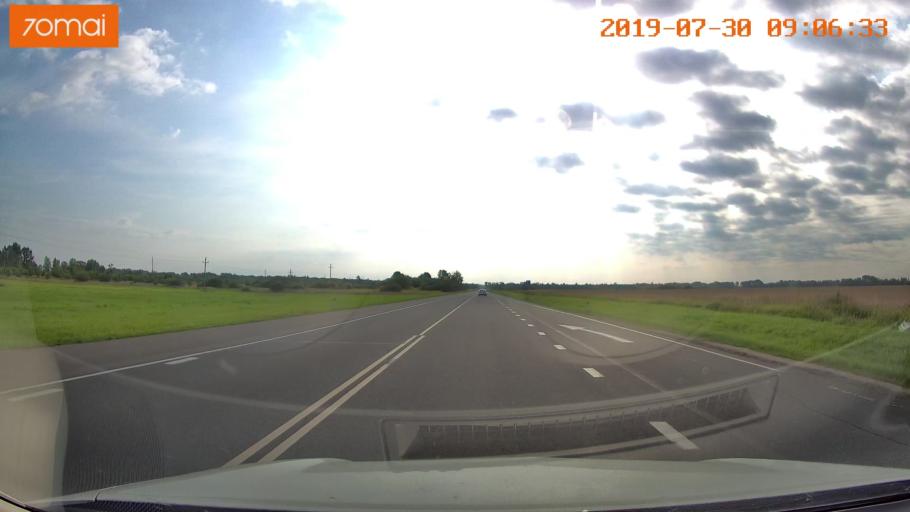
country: RU
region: Kaliningrad
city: Gusev
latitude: 54.6097
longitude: 22.3392
